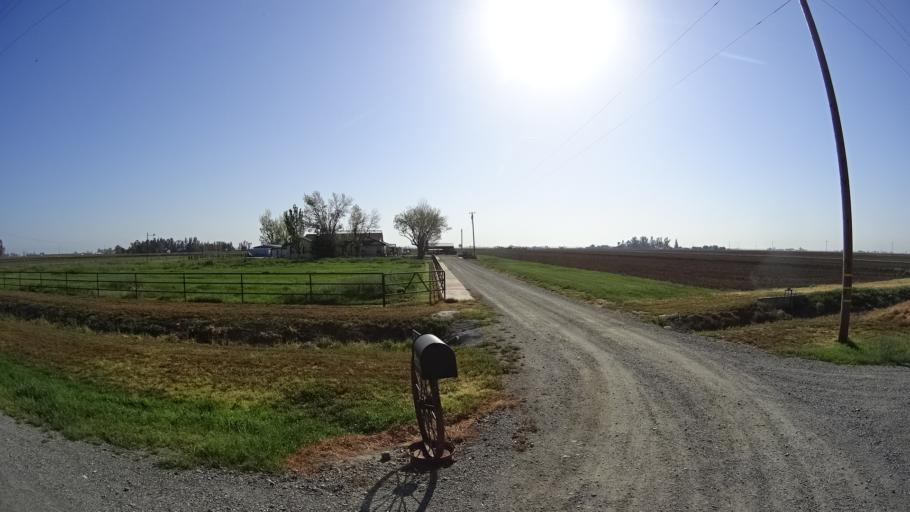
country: US
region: California
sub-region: Glenn County
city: Willows
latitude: 39.5778
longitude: -122.1077
